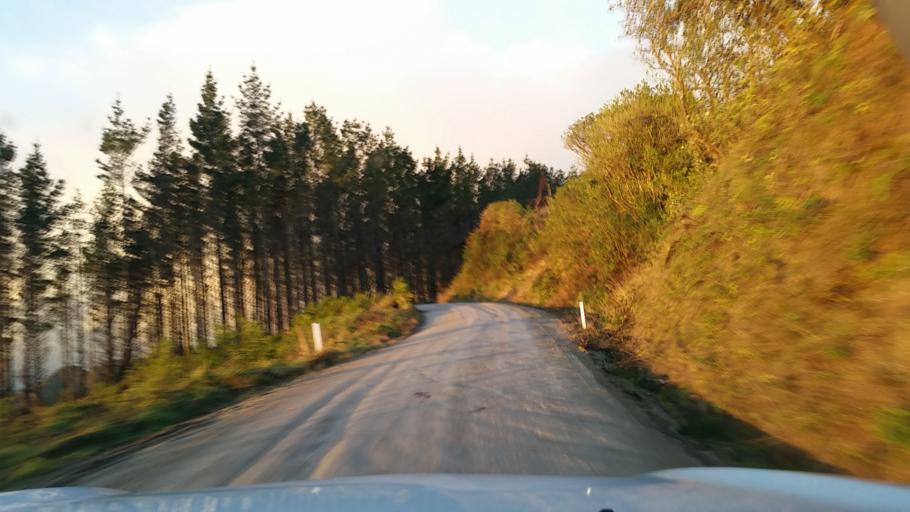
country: NZ
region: Manawatu-Wanganui
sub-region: Wanganui District
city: Wanganui
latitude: -39.7739
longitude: 174.8616
